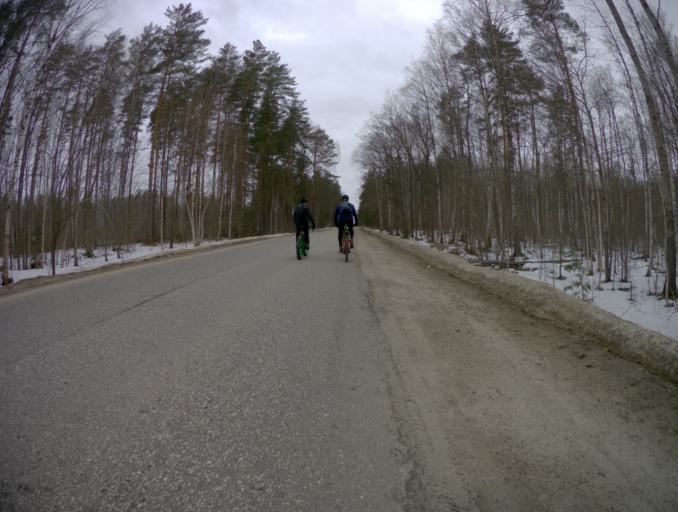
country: RU
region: Vladimir
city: Orgtrud
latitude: 56.1521
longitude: 40.5792
